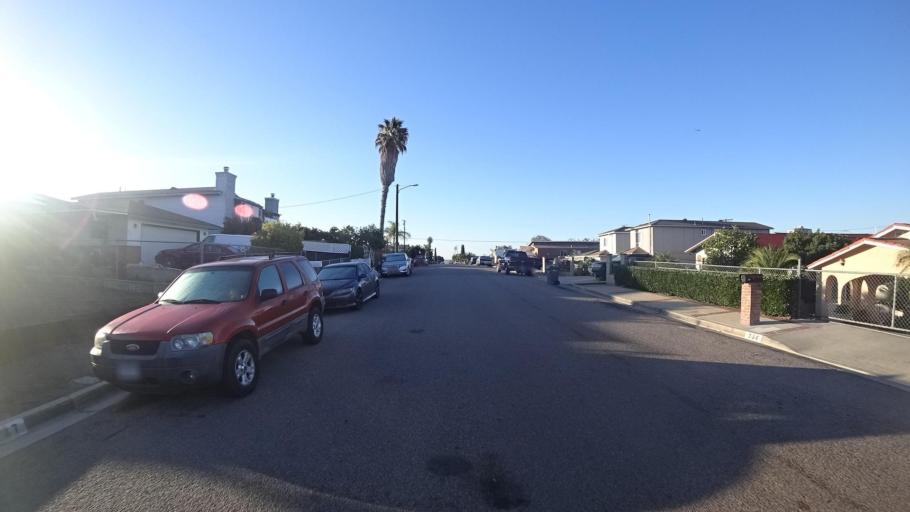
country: US
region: California
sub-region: San Diego County
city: La Presa
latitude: 32.7107
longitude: -116.9962
